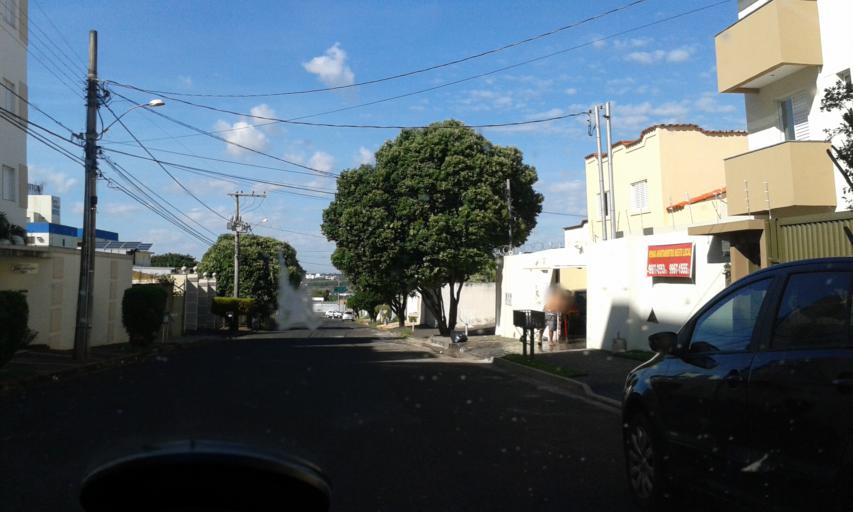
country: BR
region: Minas Gerais
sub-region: Uberlandia
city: Uberlandia
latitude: -18.9273
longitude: -48.2446
